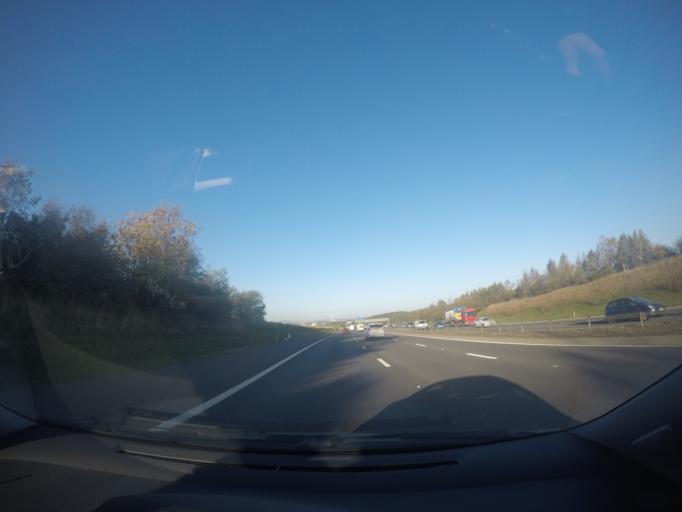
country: GB
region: England
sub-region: City and Borough of Leeds
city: Swillington
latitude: 53.7743
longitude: -1.4482
